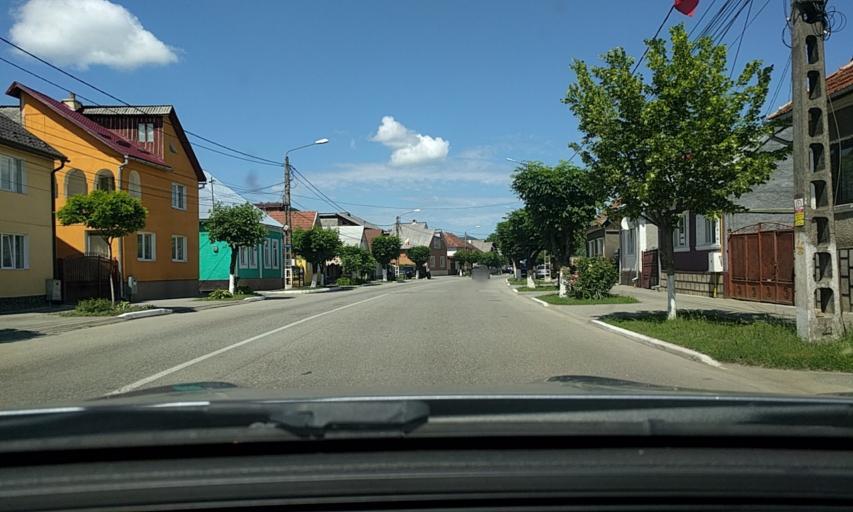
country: RO
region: Bistrita-Nasaud
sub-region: Oras Nasaud
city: Nasaud
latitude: 47.2870
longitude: 24.3968
